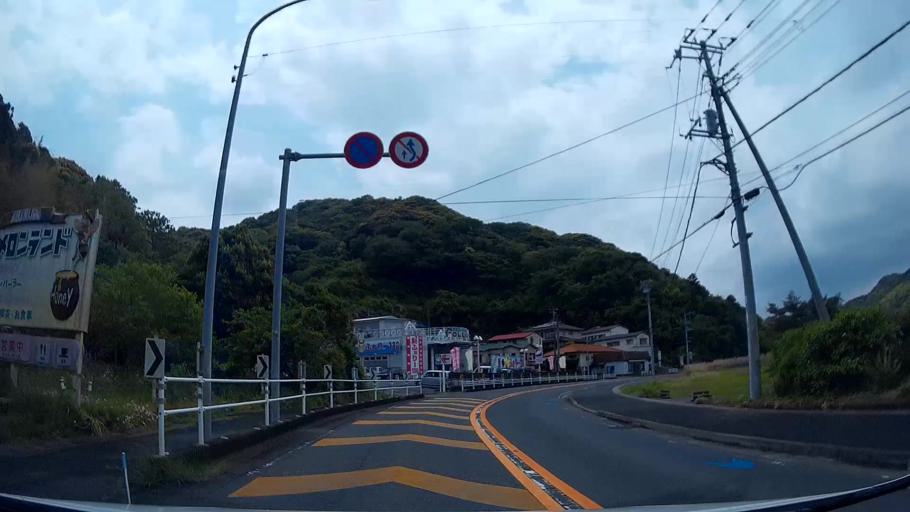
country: JP
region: Shizuoka
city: Shimoda
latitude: 34.6554
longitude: 138.8892
